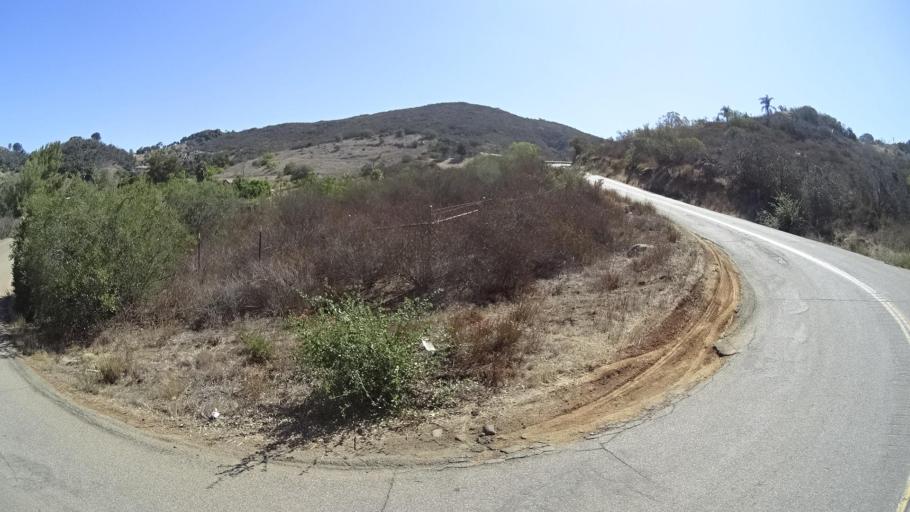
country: US
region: California
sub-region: San Diego County
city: Rainbow
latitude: 33.4156
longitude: -117.1763
